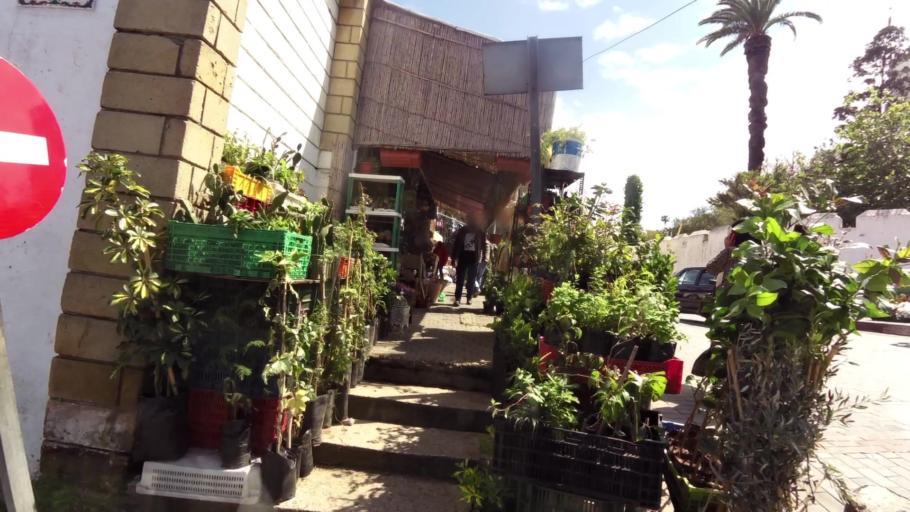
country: MA
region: Tanger-Tetouan
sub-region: Tanger-Assilah
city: Tangier
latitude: 35.7839
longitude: -5.8146
